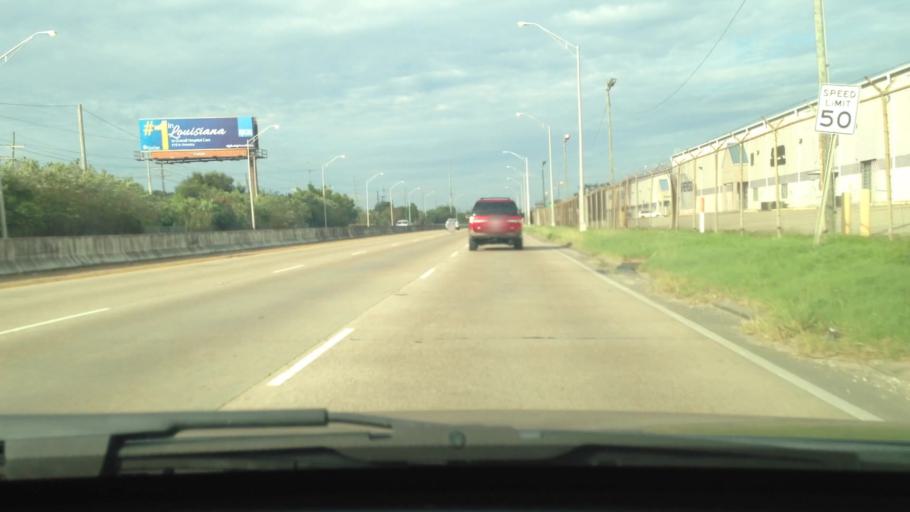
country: US
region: Louisiana
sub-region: Jefferson Parish
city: Jefferson
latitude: 29.9702
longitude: -90.1479
